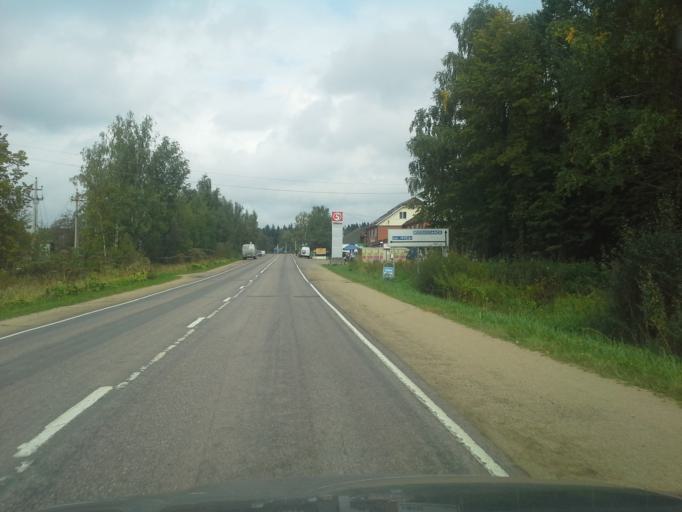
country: RU
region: Moskovskaya
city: Ruza
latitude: 55.7573
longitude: 36.1444
